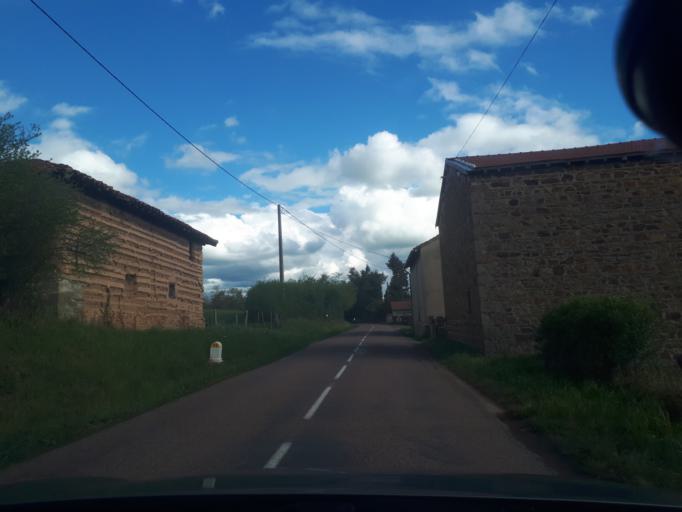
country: FR
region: Rhone-Alpes
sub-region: Departement de la Loire
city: Pouilly-les-Feurs
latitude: 45.8084
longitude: 4.2214
